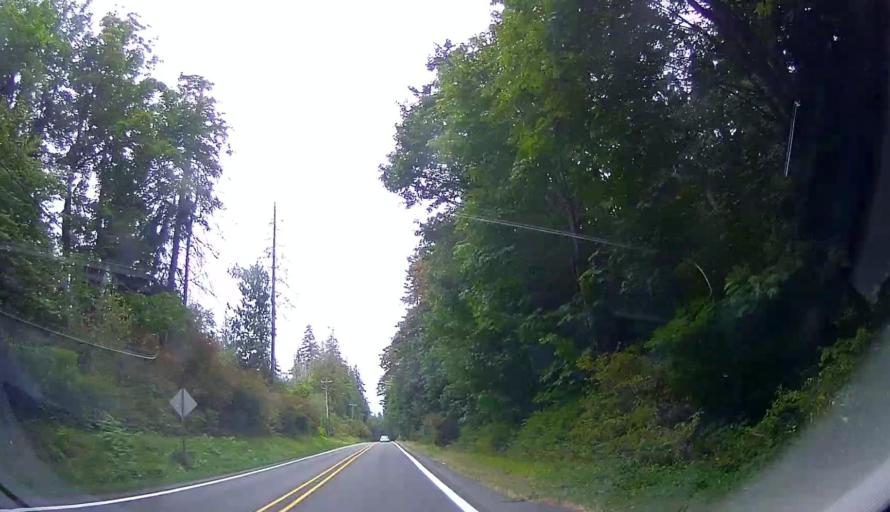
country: US
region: Washington
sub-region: Snohomish County
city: Warm Beach
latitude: 48.1305
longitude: -122.3570
